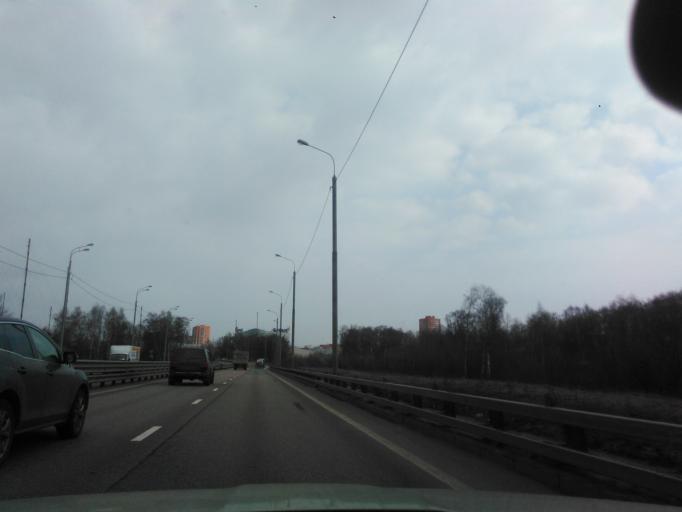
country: RU
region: Moscow
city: Khimki
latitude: 55.8792
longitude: 37.4055
